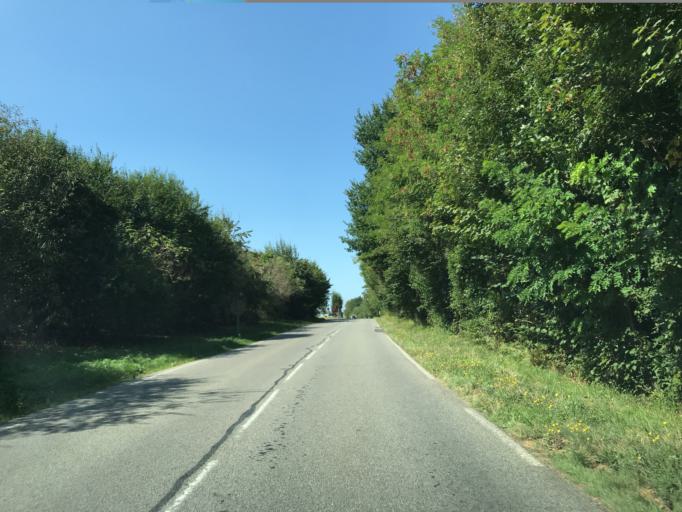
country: FR
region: Haute-Normandie
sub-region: Departement de l'Eure
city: La Chapelle-Reanville
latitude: 49.0944
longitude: 1.3932
